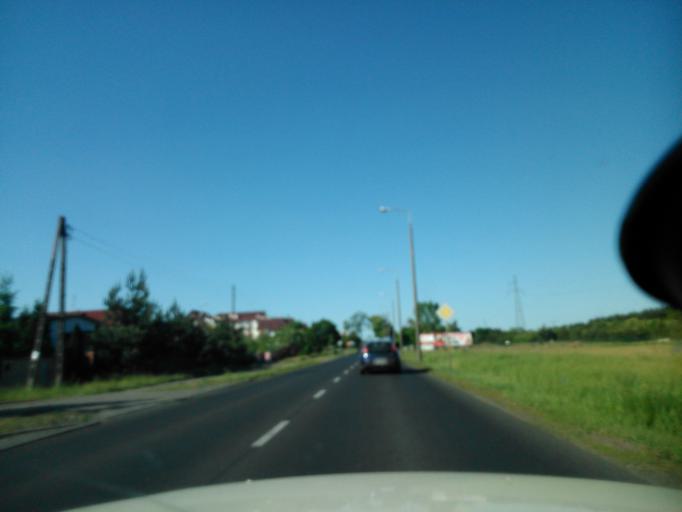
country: PL
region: Kujawsko-Pomorskie
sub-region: Torun
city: Torun
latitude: 52.9792
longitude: 18.5717
